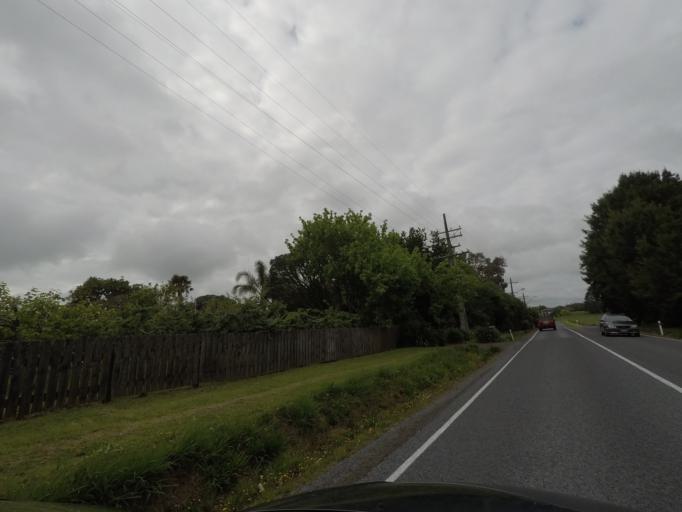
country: NZ
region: Auckland
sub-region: Auckland
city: Rosebank
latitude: -36.7988
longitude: 174.5739
